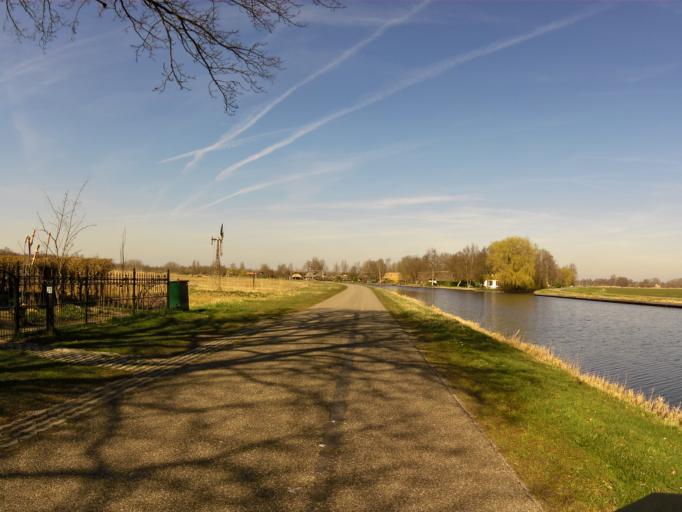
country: NL
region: Overijssel
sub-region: Gemeente Steenwijkerland
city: Oldemarkt
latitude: 52.8074
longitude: 5.9414
